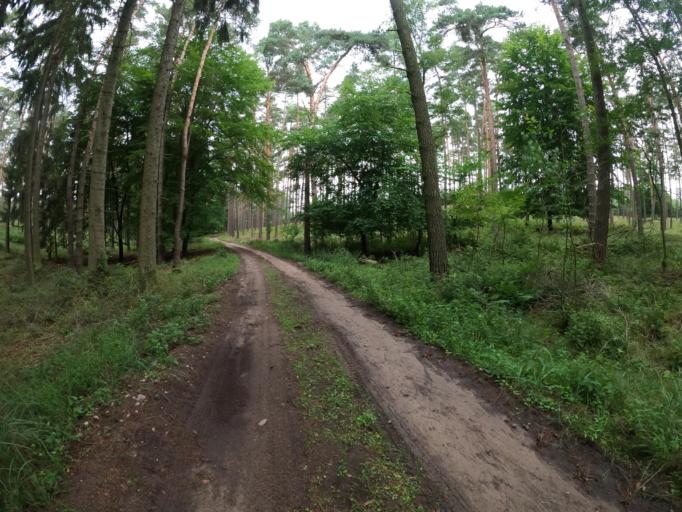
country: DE
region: Brandenburg
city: Althuttendorf
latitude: 53.0361
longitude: 13.8874
